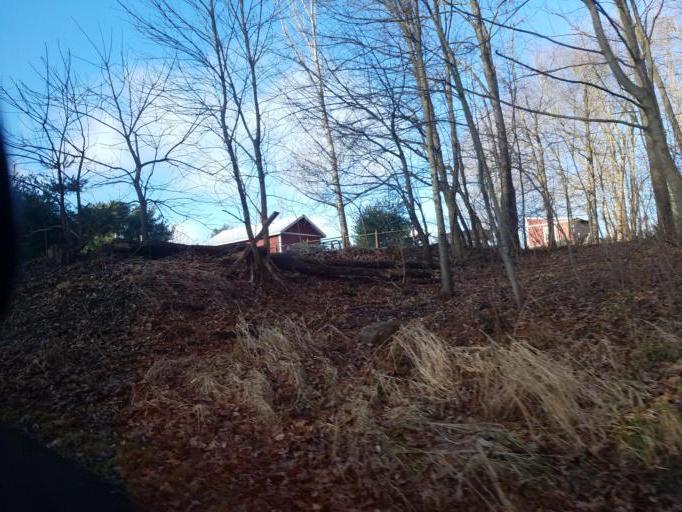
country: US
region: Ohio
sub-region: Sandusky County
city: Bellville
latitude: 40.5830
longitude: -82.5446
